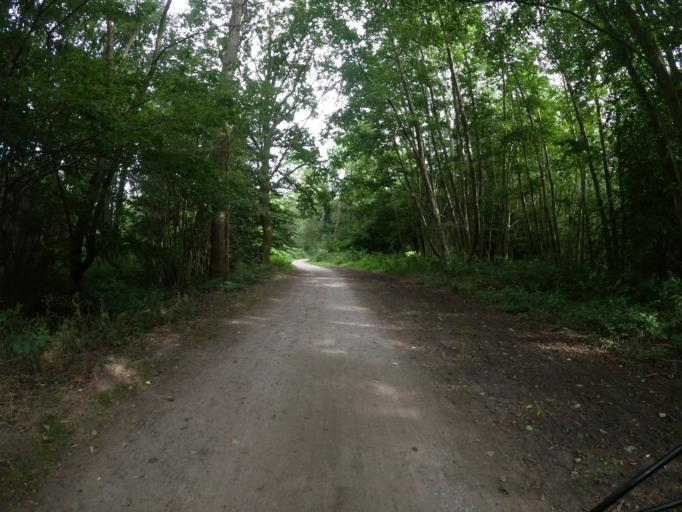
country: DE
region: North Rhine-Westphalia
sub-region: Regierungsbezirk Arnsberg
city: Lippstadt
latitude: 51.6948
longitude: 8.3288
